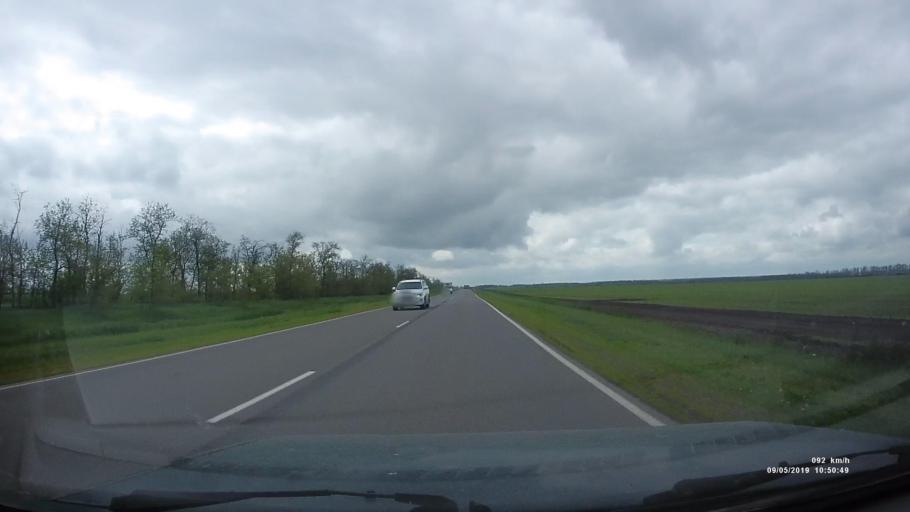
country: RU
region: Rostov
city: Peshkovo
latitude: 46.9233
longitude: 39.3553
